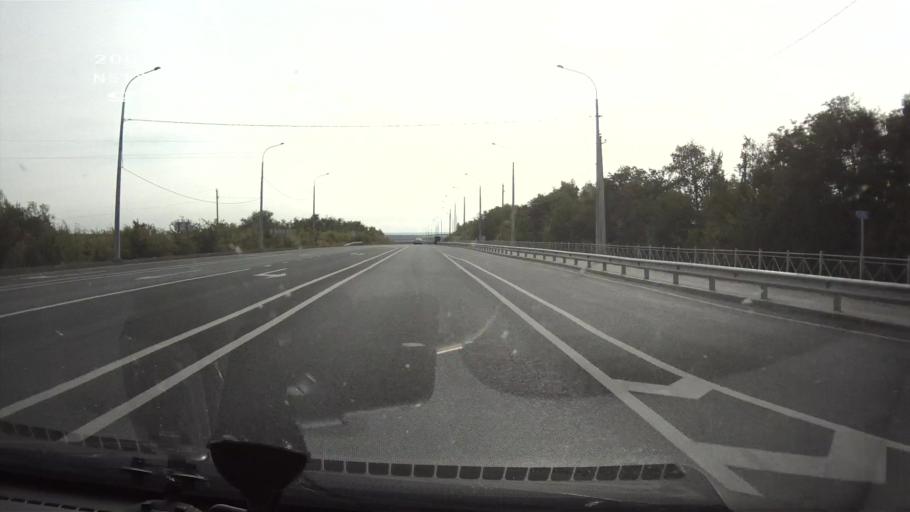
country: RU
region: Saratov
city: Yelshanka
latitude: 51.8942
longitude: 46.5285
